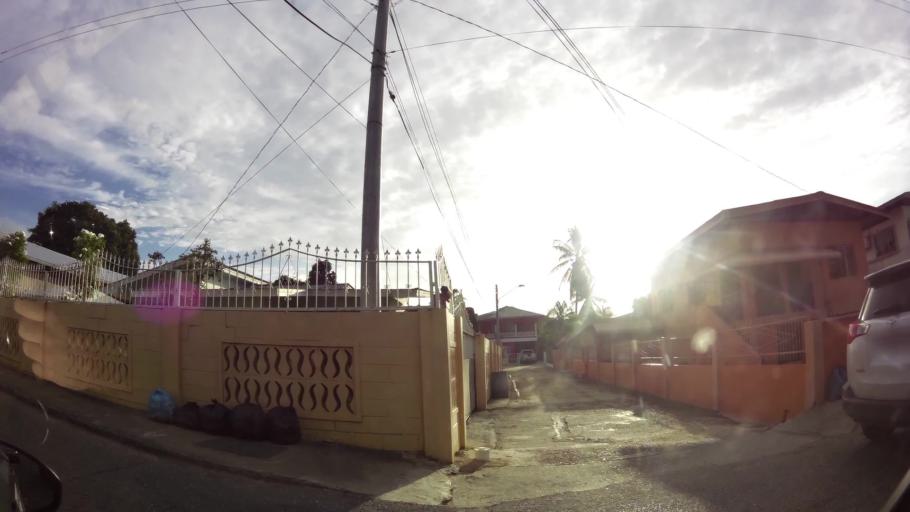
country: TT
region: Tunapuna/Piarco
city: Tunapuna
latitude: 10.6414
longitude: -61.4026
